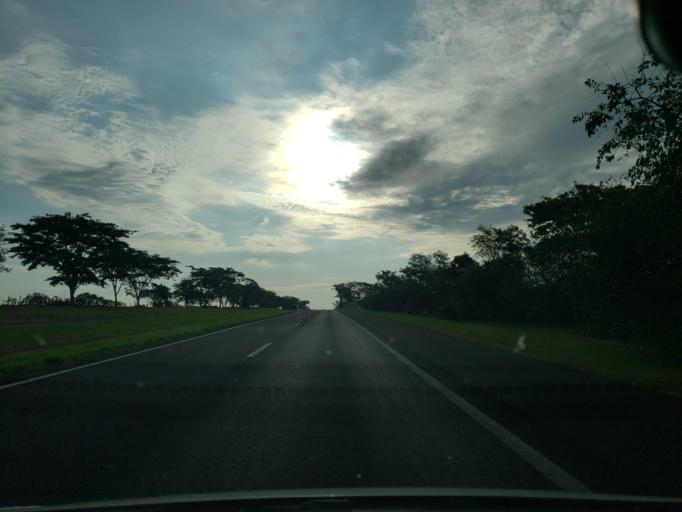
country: BR
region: Sao Paulo
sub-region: Mirandopolis
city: Mirandopolis
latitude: -21.1137
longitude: -51.0192
